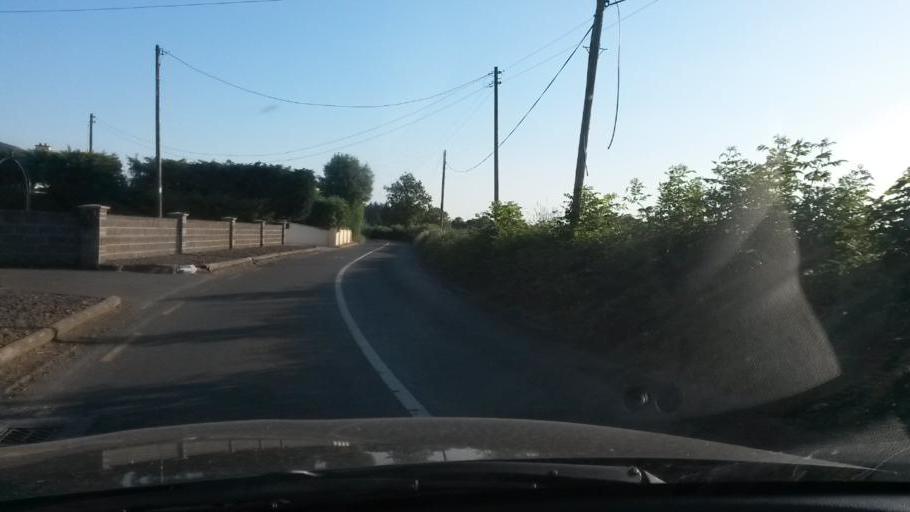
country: IE
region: Leinster
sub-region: Fingal County
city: Blanchardstown
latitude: 53.4356
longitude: -6.3577
